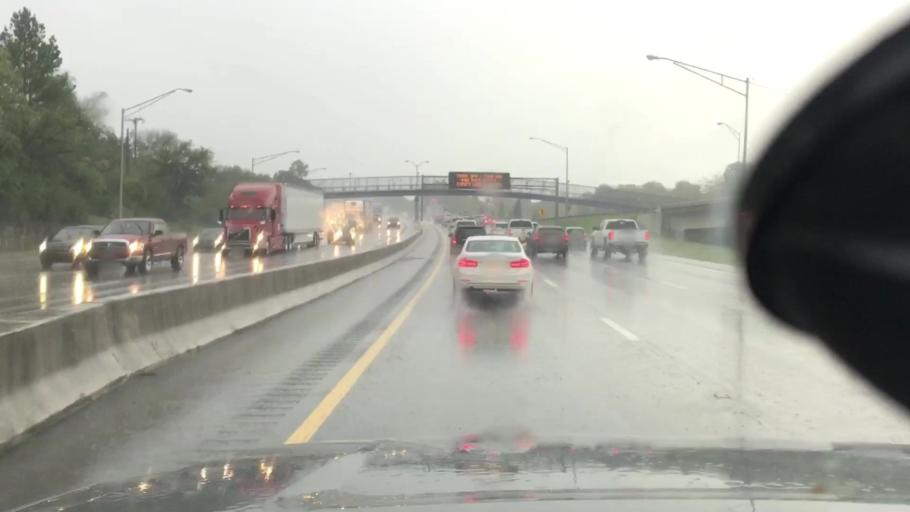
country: US
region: Tennessee
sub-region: Davidson County
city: Nashville
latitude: 36.1678
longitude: -86.8164
